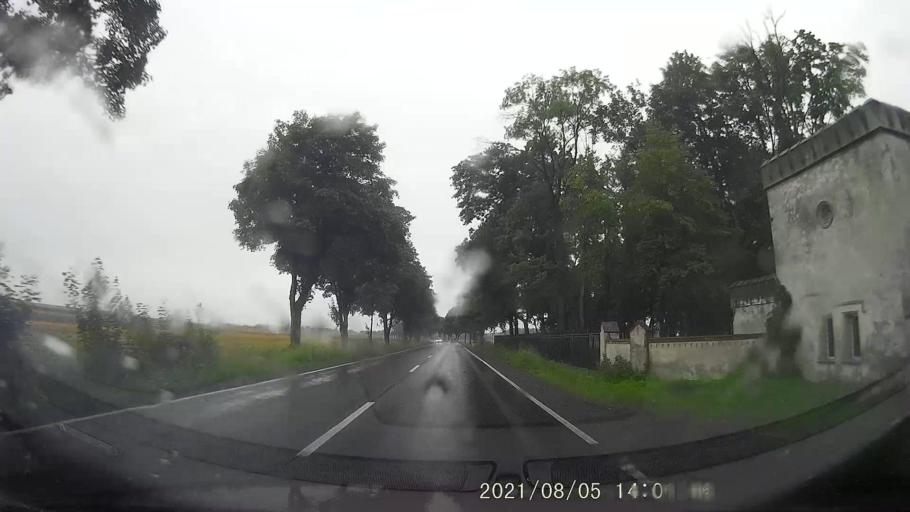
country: PL
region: Opole Voivodeship
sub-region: Powiat krapkowicki
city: Strzeleczki
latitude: 50.4500
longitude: 17.8877
